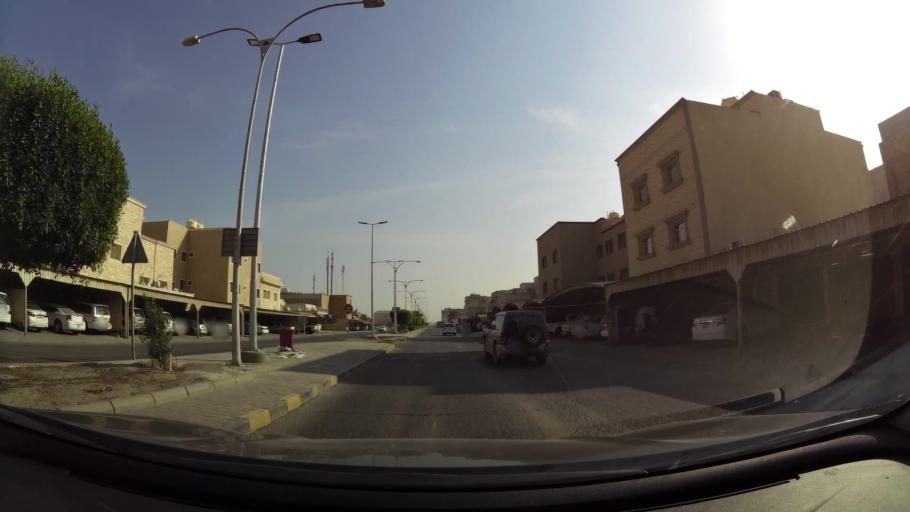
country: KW
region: Al Ahmadi
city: Ar Riqqah
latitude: 29.1421
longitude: 48.1075
